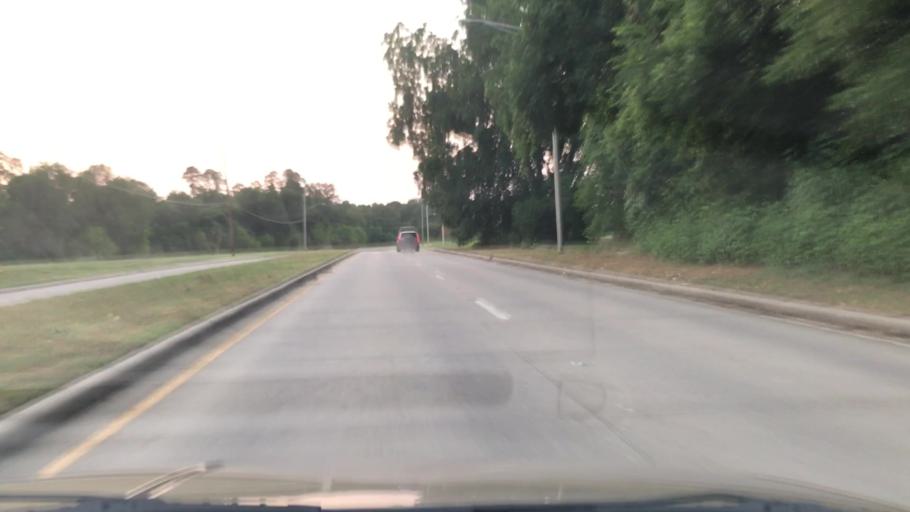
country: US
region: Louisiana
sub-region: Bossier Parish
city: Bossier City
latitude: 32.4349
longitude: -93.7271
